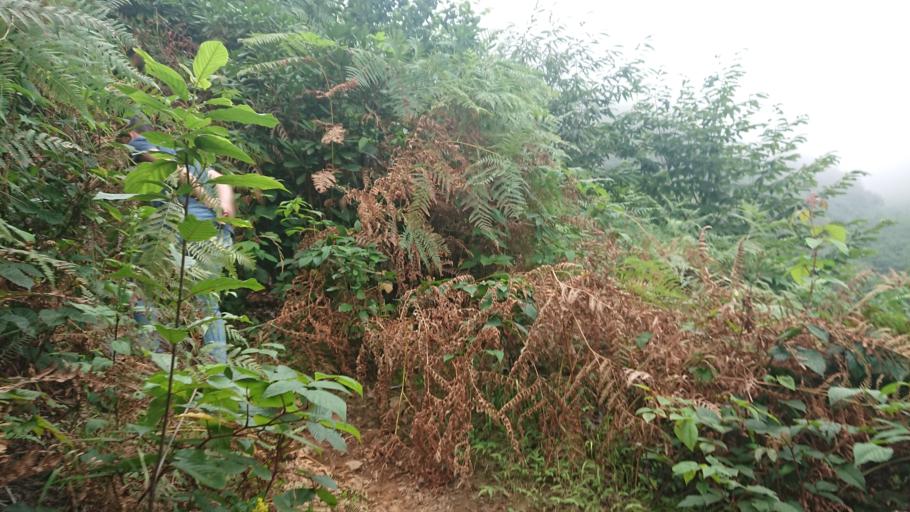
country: TR
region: Rize
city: Hemsin
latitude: 41.0457
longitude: 40.8085
